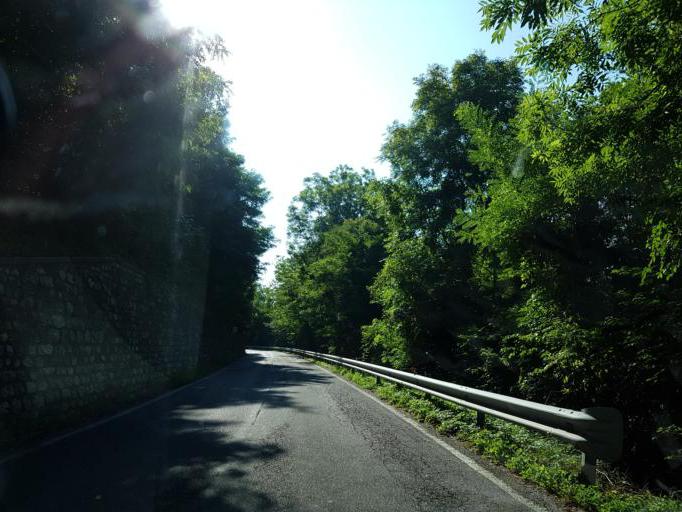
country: IT
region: Piedmont
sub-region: Provincia di Cuneo
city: Cartignano
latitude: 44.4704
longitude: 7.3135
